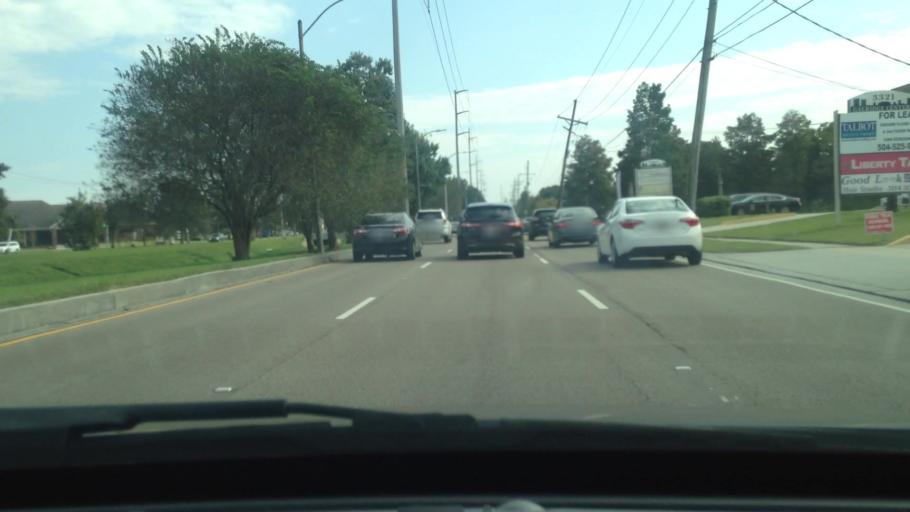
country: US
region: Louisiana
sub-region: Jefferson Parish
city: Terrytown
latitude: 29.9267
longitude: -90.0261
